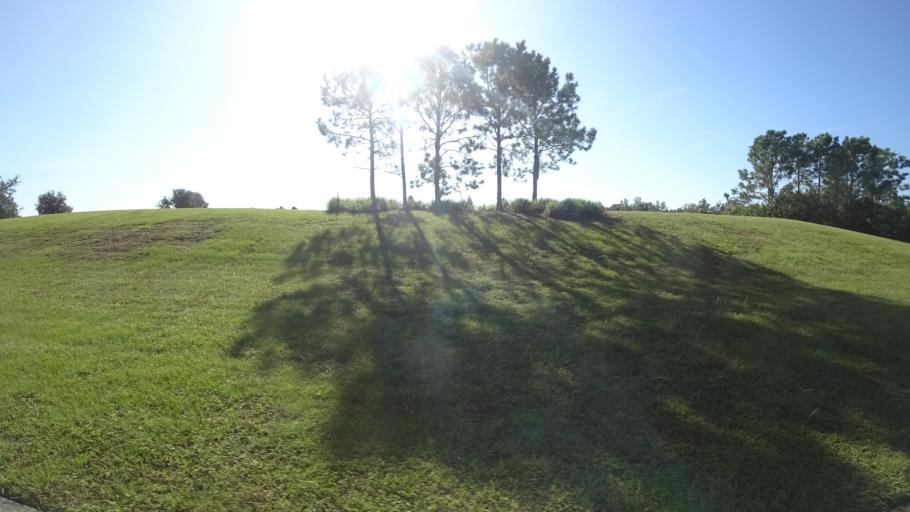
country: US
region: Florida
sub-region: Sarasota County
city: The Meadows
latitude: 27.4204
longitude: -82.4184
